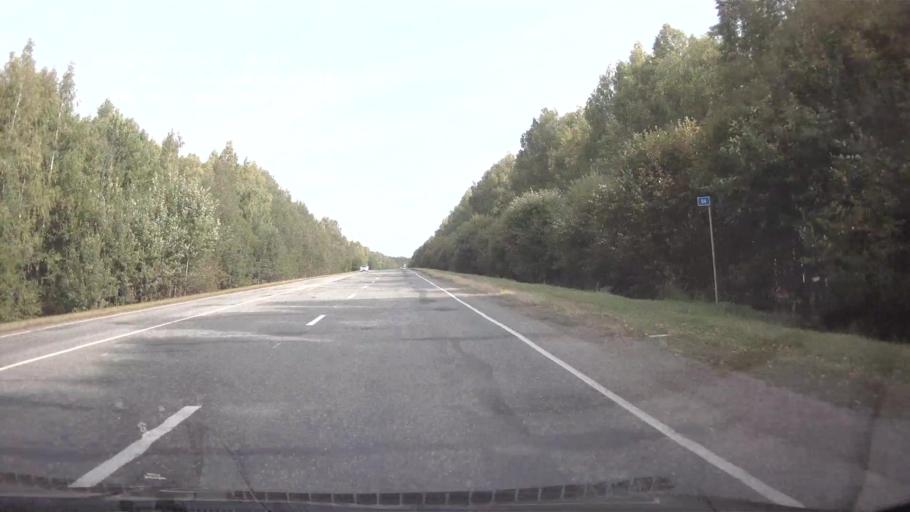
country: RU
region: Mariy-El
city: Sovetskiy
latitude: 56.8012
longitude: 48.6891
